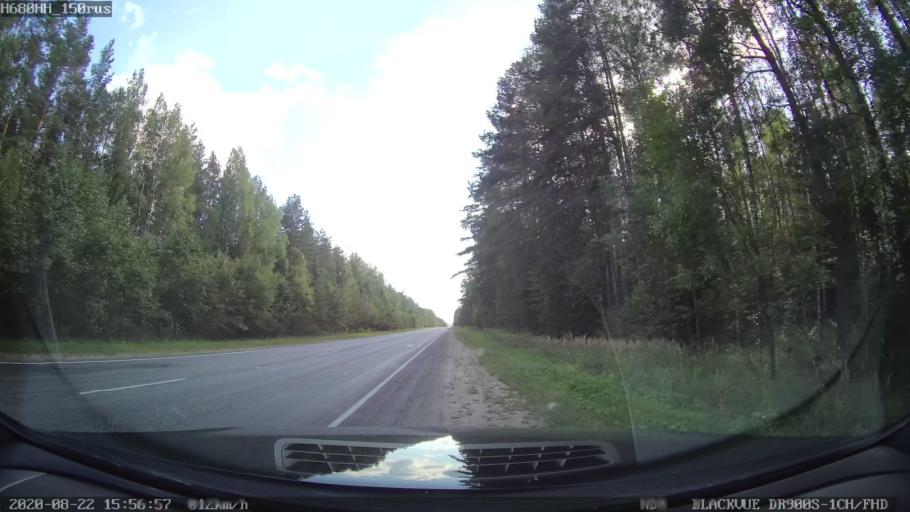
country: RU
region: Tverskaya
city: Bezhetsk
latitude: 57.6100
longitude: 36.3631
